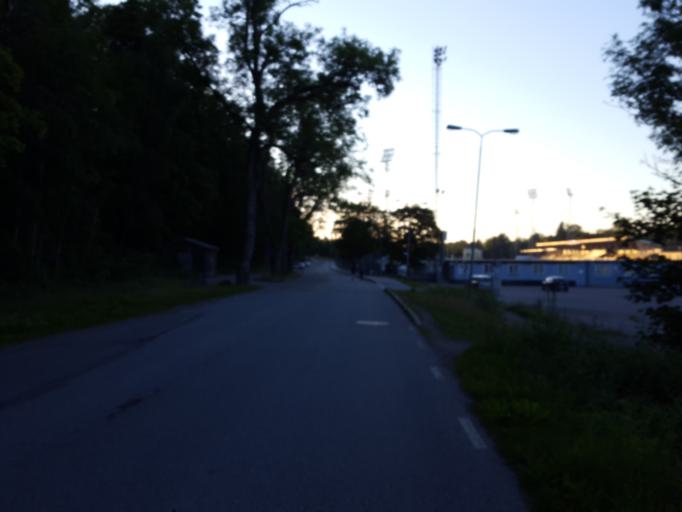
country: SE
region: Uppsala
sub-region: Uppsala Kommun
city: Uppsala
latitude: 59.8456
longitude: 17.6489
